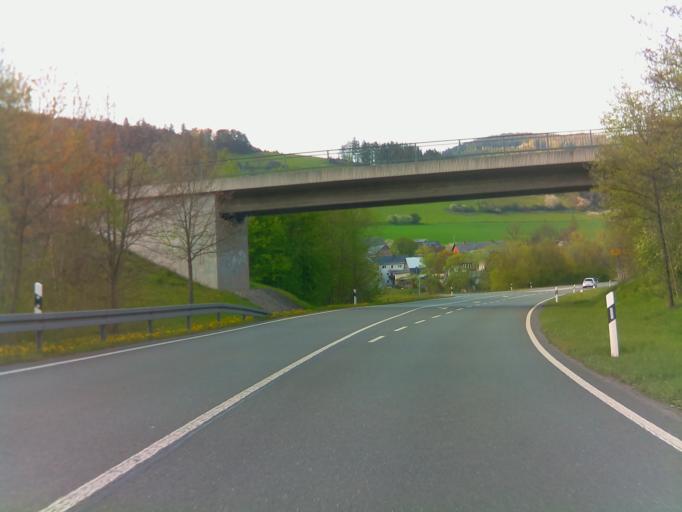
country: DE
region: Thuringia
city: Probstzella
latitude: 50.5609
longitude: 11.3493
